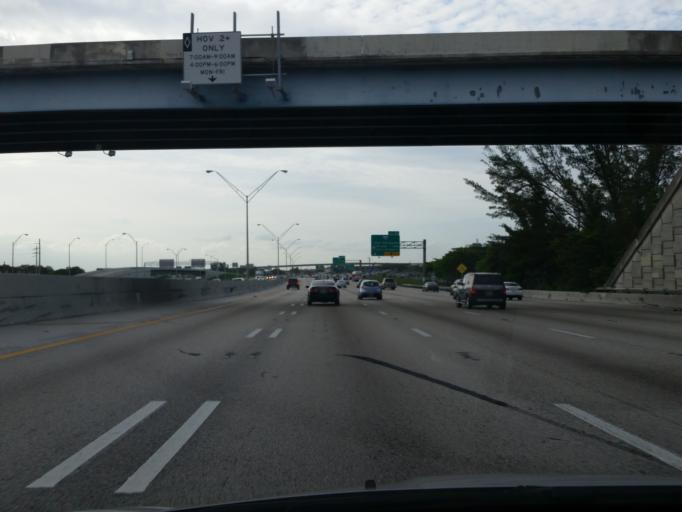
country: US
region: Florida
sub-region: Broward County
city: Dania Beach
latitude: 26.0700
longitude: -80.1661
